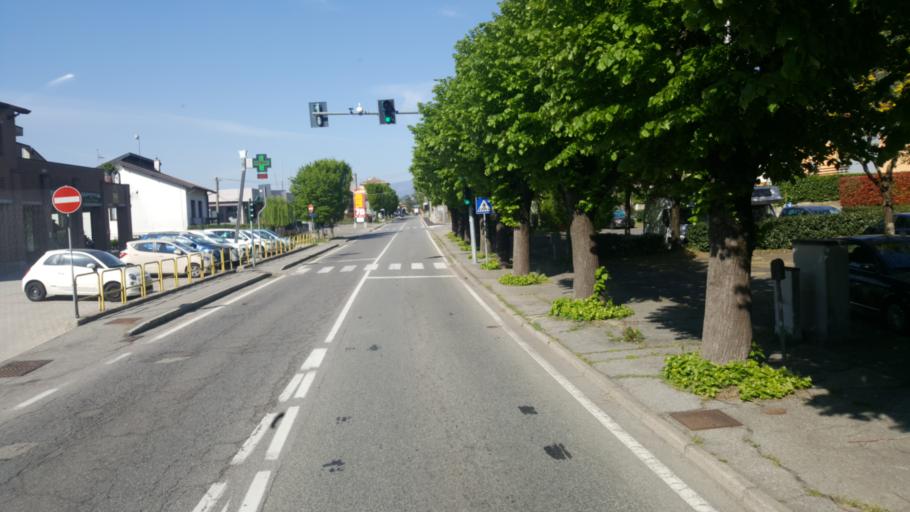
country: IT
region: Lombardy
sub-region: Provincia di Varese
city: Cuveglio
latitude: 45.9051
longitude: 8.7405
